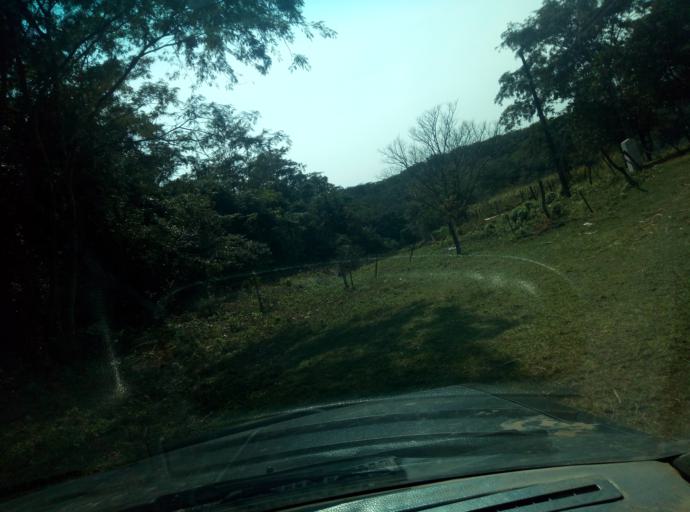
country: PY
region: Caaguazu
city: Carayao
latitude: -25.3019
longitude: -56.3226
